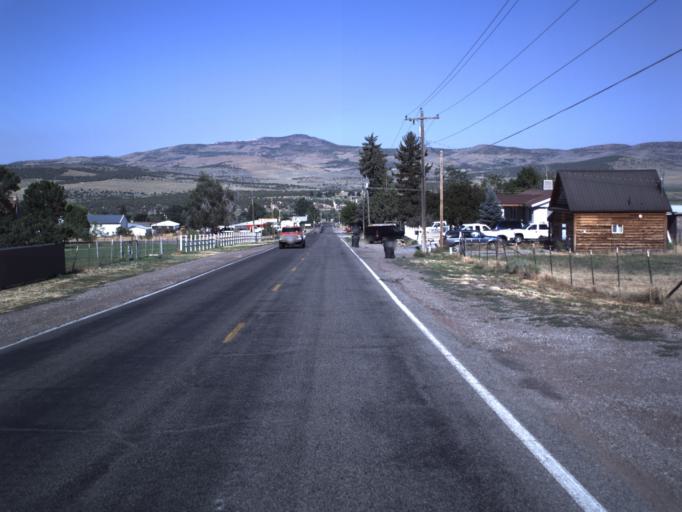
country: US
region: Utah
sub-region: Sanpete County
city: Fairview
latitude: 39.6344
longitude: -111.4313
